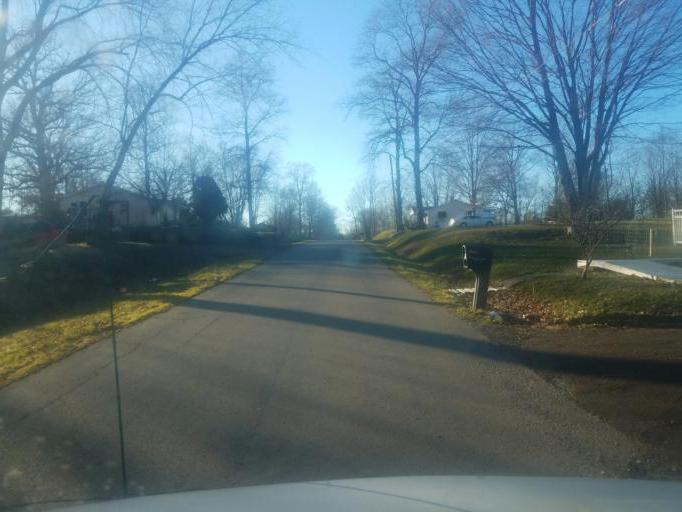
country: US
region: Ohio
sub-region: Richland County
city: Mansfield
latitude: 40.7885
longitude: -82.5346
